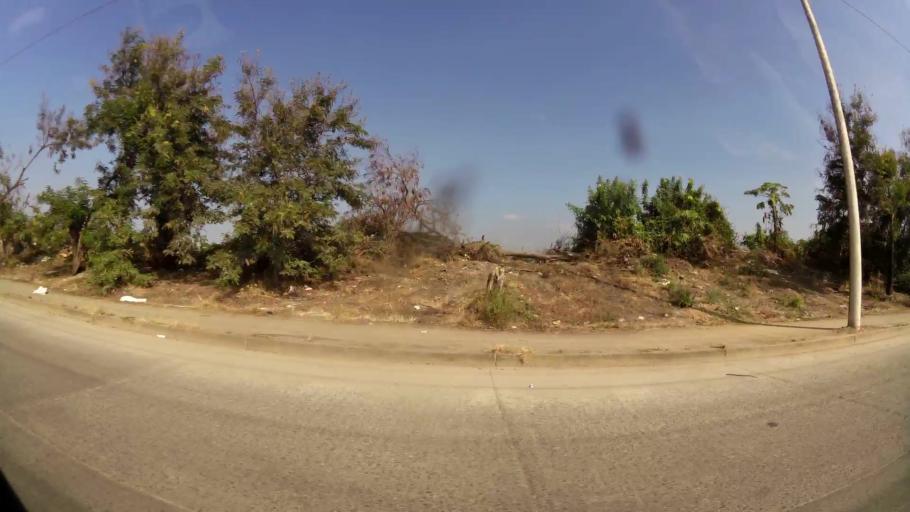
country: EC
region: Guayas
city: Eloy Alfaro
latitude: -2.1679
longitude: -79.8064
